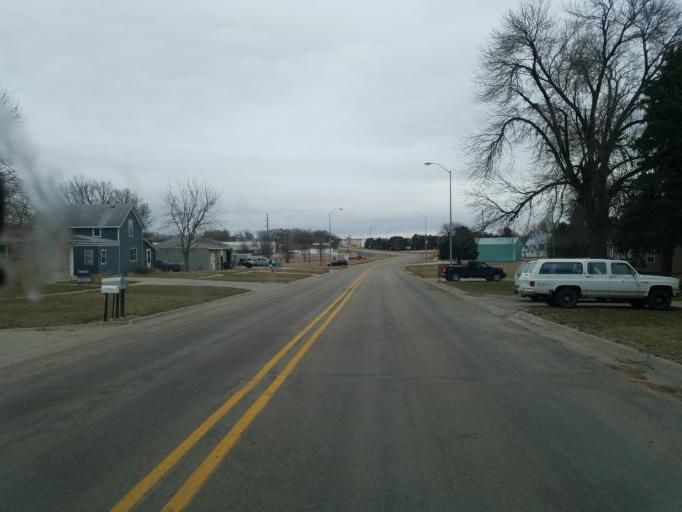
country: US
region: Nebraska
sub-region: Knox County
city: Bloomfield
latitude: 42.5982
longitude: -97.6399
